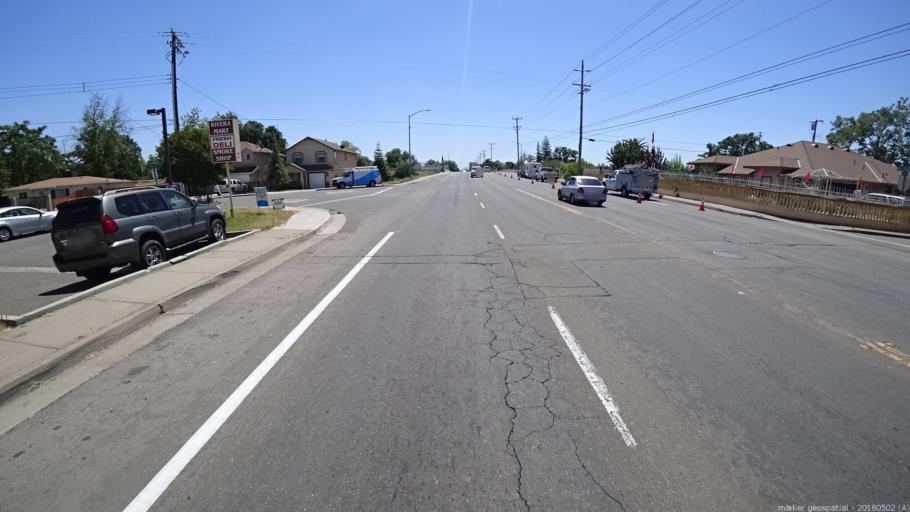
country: US
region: California
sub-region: Sacramento County
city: Rio Linda
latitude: 38.6273
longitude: -121.4461
